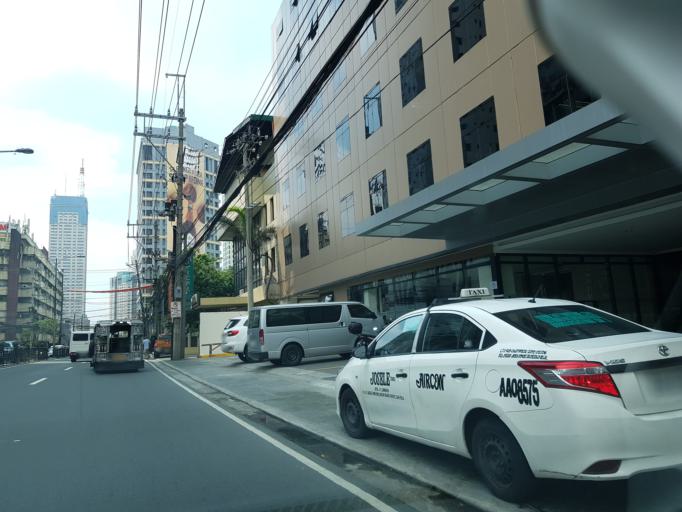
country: PH
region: Metro Manila
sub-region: Mandaluyong
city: Mandaluyong City
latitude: 14.5838
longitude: 121.0507
